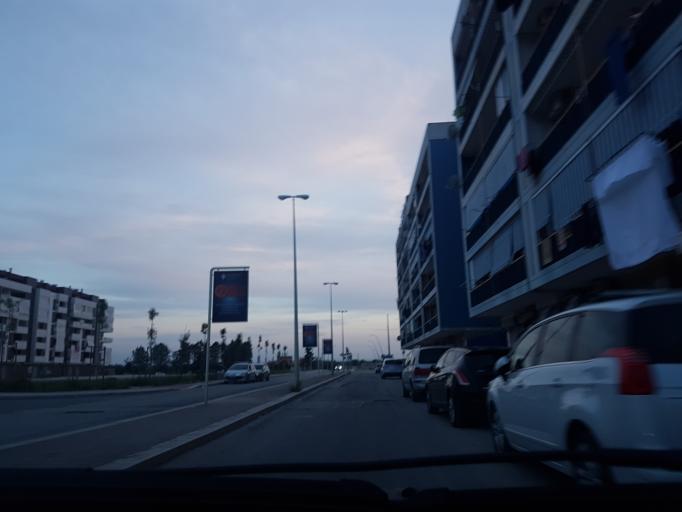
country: IT
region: Apulia
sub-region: Provincia di Barletta - Andria - Trani
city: Barletta
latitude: 41.3063
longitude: 16.2647
